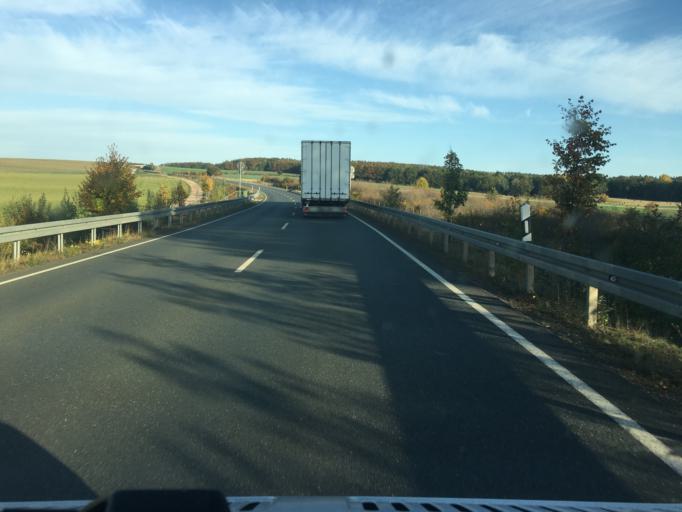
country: DE
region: Saxony
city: Lichtentanne
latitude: 50.7163
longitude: 12.4214
